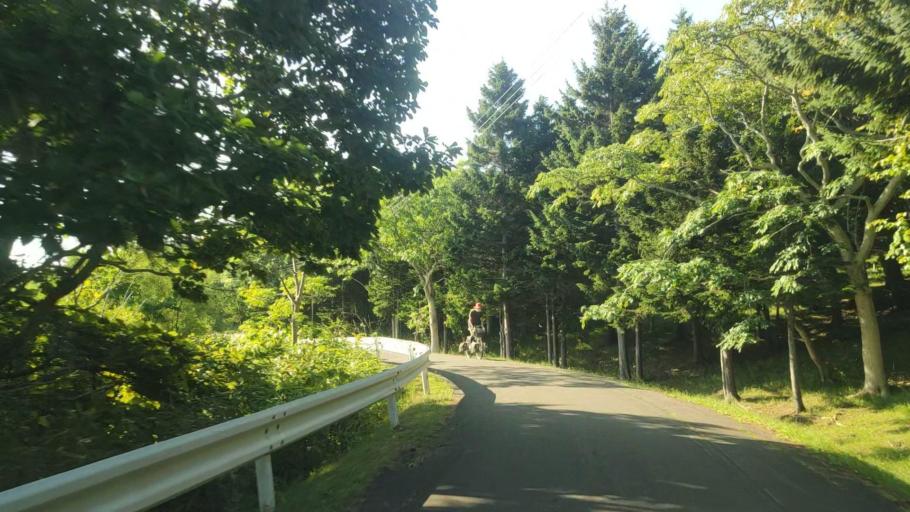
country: JP
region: Hokkaido
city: Wakkanai
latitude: 45.4134
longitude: 141.6688
